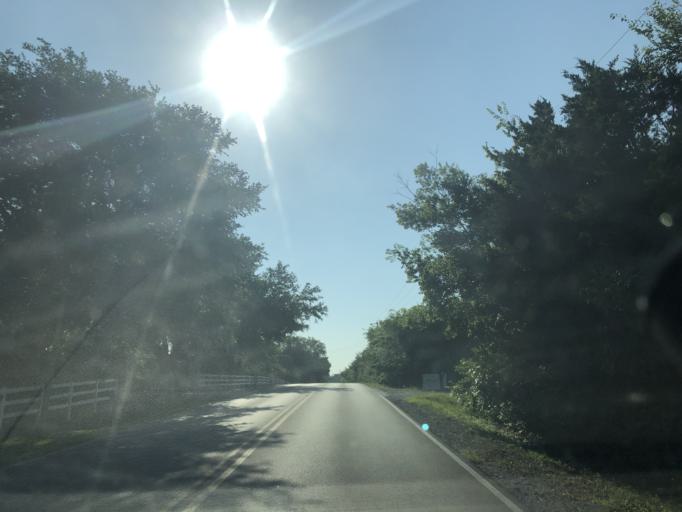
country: US
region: Texas
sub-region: Dallas County
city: Sunnyvale
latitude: 32.8140
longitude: -96.5853
